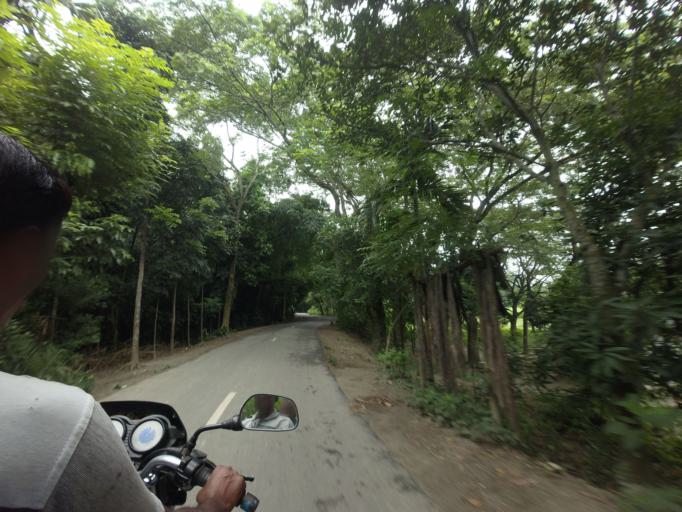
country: BD
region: Khulna
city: Kalia
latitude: 23.1310
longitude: 89.6433
